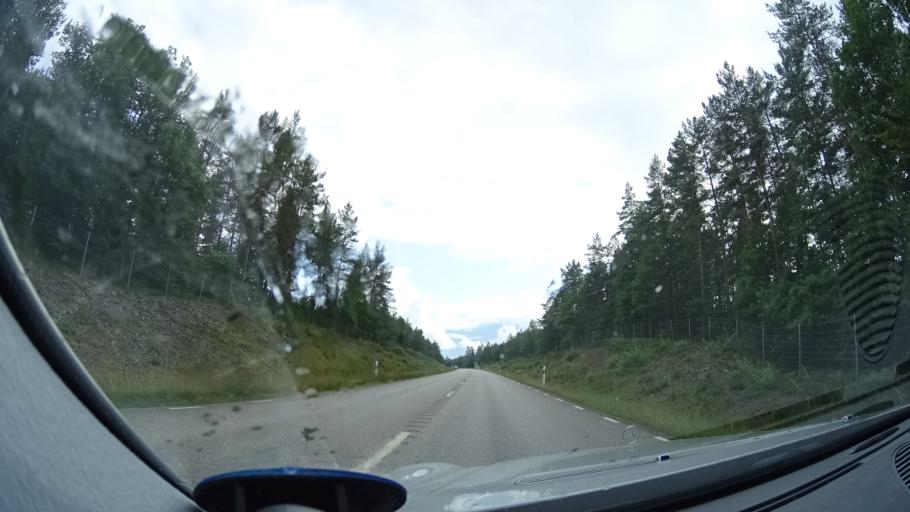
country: SE
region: Blekinge
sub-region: Karlshamns Kommun
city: Svangsta
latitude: 56.2548
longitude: 14.8322
